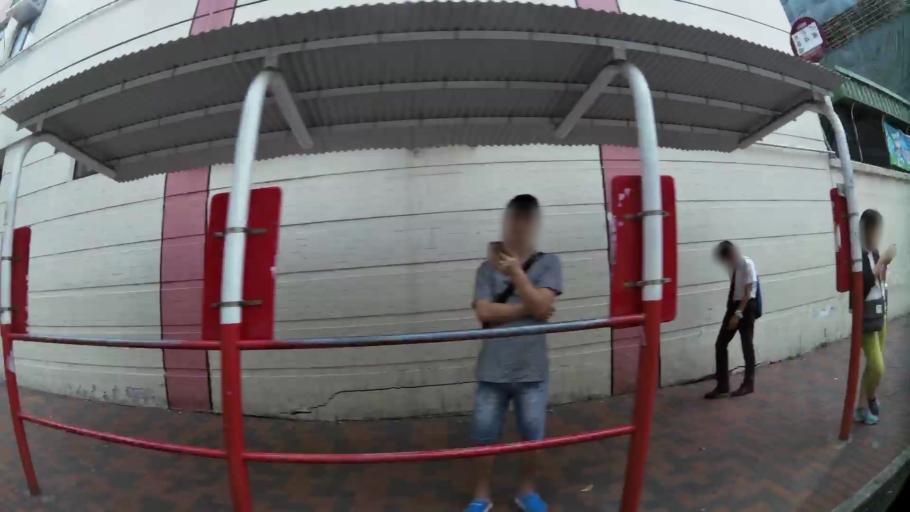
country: HK
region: Kowloon City
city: Kowloon
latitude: 22.3311
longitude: 114.1871
